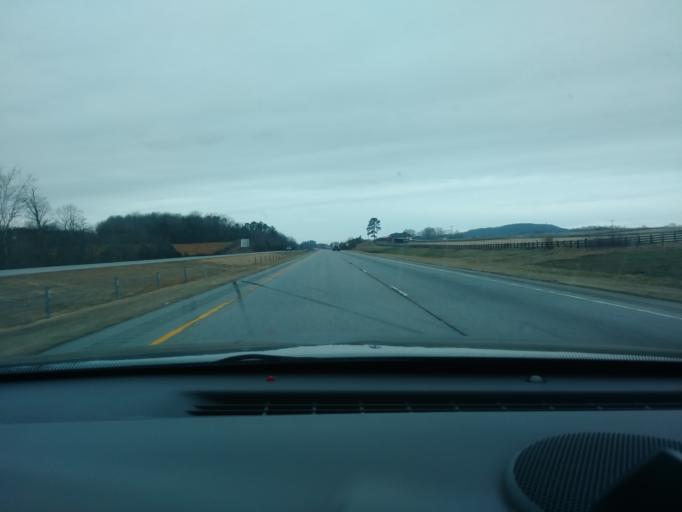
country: US
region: North Carolina
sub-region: Yadkin County
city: Jonesville
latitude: 36.1337
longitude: -80.8513
